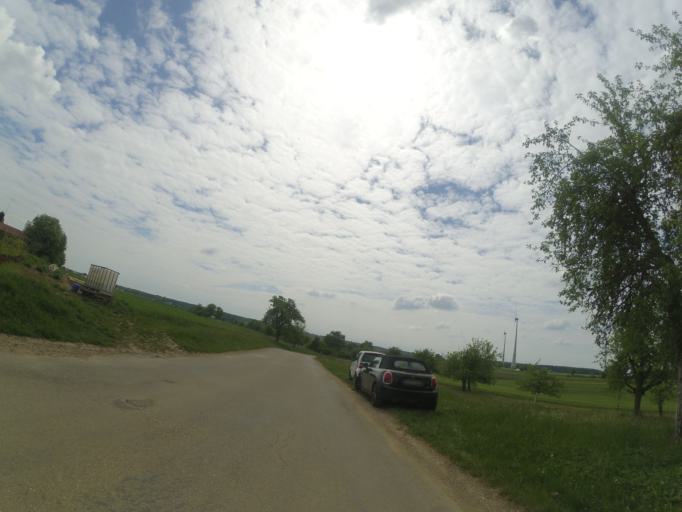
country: DE
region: Baden-Wuerttemberg
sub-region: Tuebingen Region
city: Berghulen
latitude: 48.4592
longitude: 9.7616
